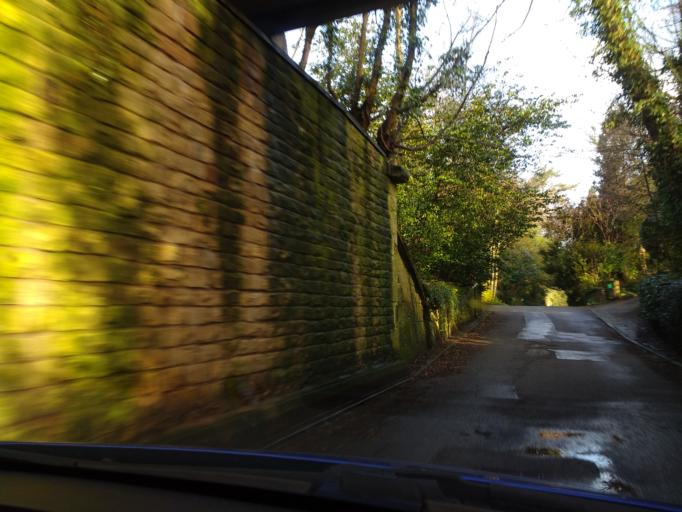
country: GB
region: England
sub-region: Lancashire
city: Caton
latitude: 54.0762
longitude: -2.7242
